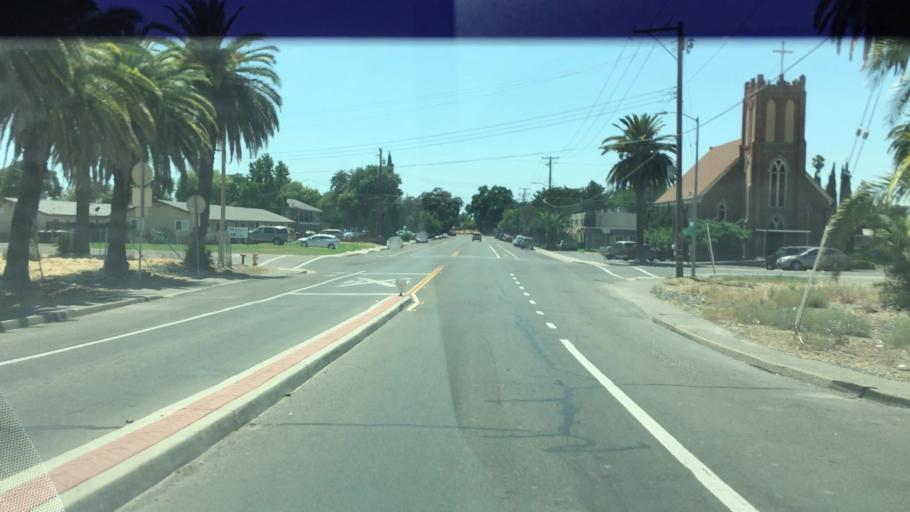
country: US
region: California
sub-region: Sacramento County
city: Galt
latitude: 38.2489
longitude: -121.3055
